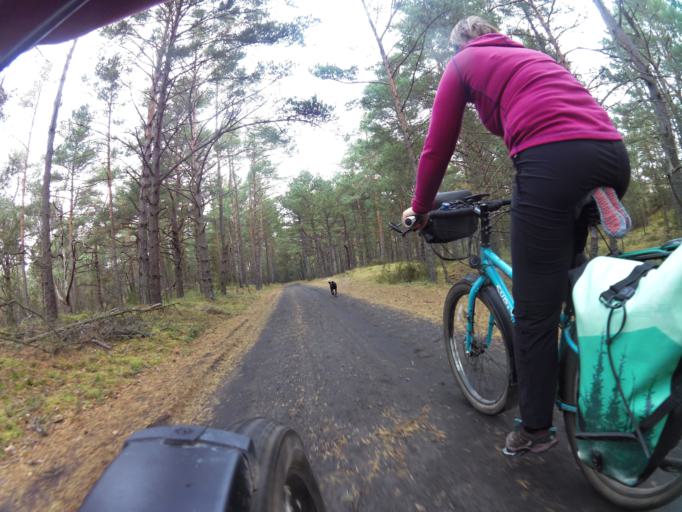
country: PL
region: Pomeranian Voivodeship
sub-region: Powiat pucki
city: Hel
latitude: 54.6205
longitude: 18.8198
